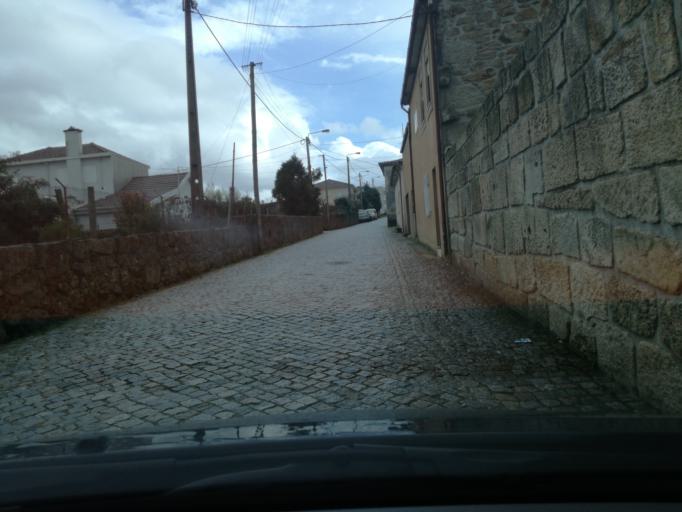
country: PT
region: Porto
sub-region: Valongo
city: Ermesinde
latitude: 41.2431
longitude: -8.5487
